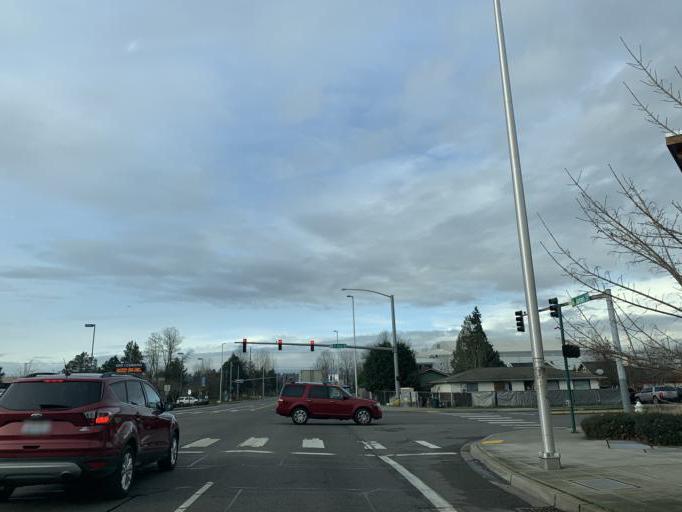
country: US
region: Washington
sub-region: King County
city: Kent
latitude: 47.3867
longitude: -122.2368
